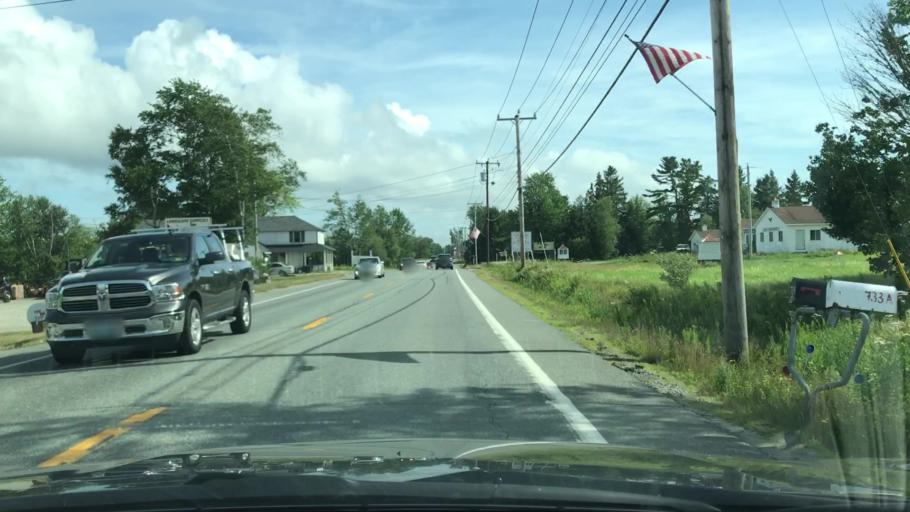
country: US
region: Maine
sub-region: Hancock County
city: Trenton
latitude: 44.4655
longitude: -68.3622
